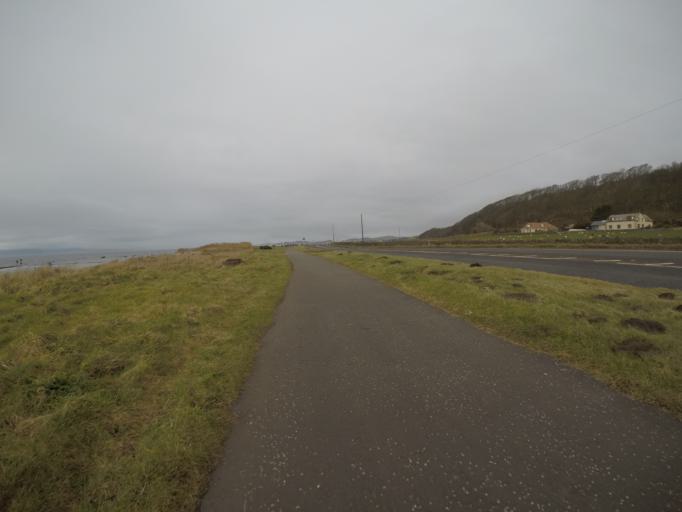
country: GB
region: Scotland
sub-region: North Ayrshire
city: West Kilbride
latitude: 55.6681
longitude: -4.8422
